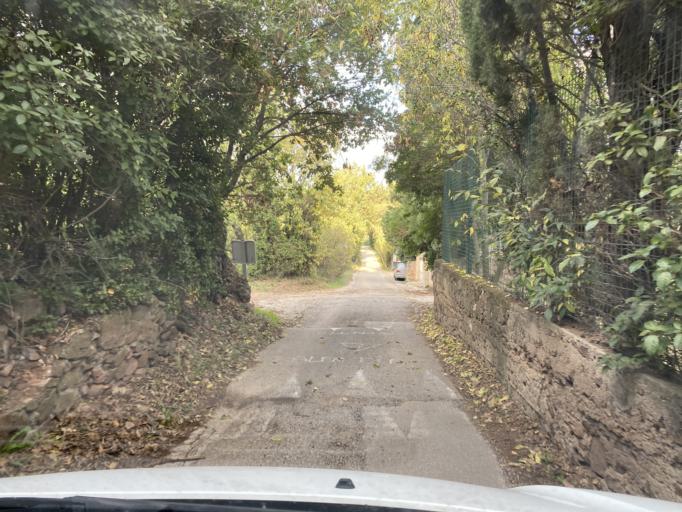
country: FR
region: Provence-Alpes-Cote d'Azur
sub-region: Departement du Var
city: La Seyne-sur-Mer
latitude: 43.1218
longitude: 5.8733
